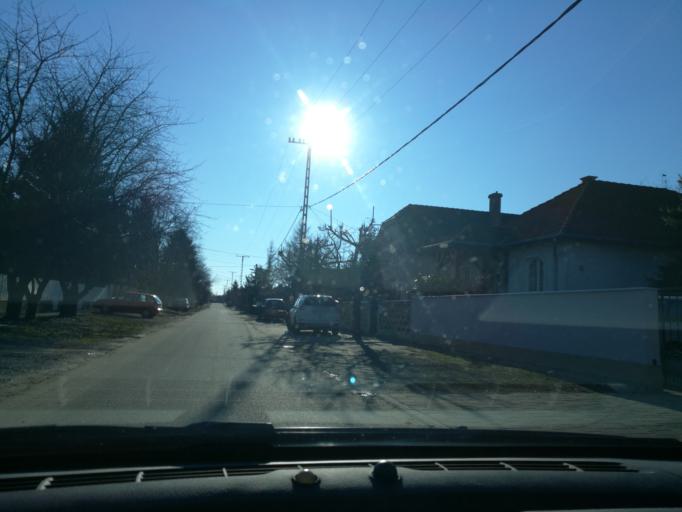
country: HU
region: Szabolcs-Szatmar-Bereg
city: Nyiregyhaza
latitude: 47.9493
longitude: 21.7520
